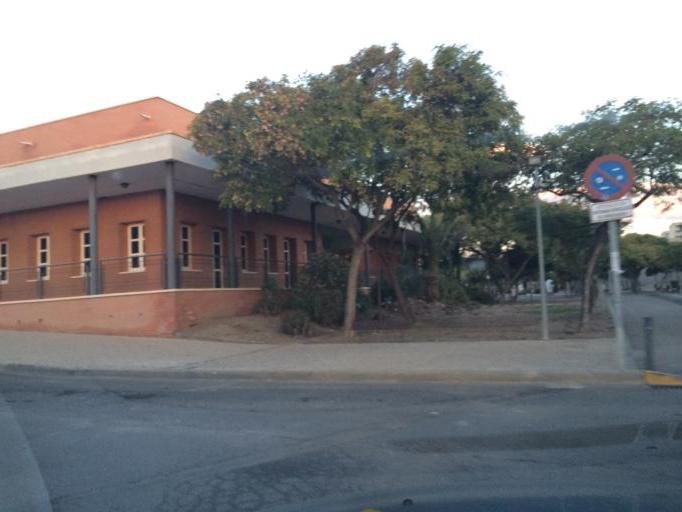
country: ES
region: Andalusia
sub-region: Provincia de Almeria
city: Almeria
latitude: 36.8280
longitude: -2.4053
